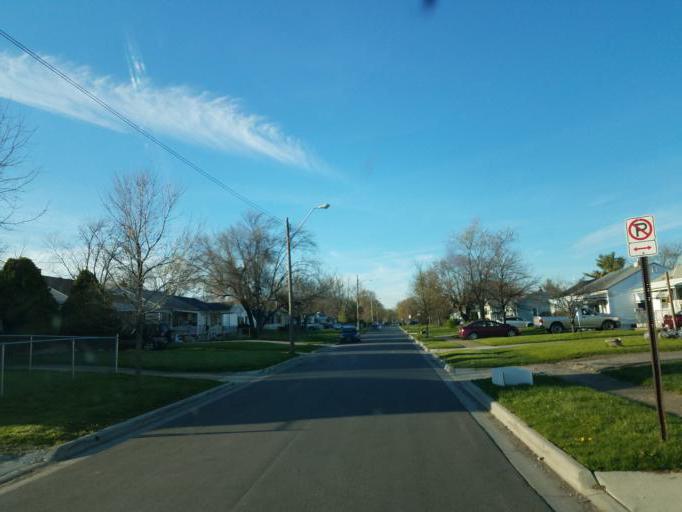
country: US
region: Ohio
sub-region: Franklin County
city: Columbus
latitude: 40.0167
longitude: -82.9909
